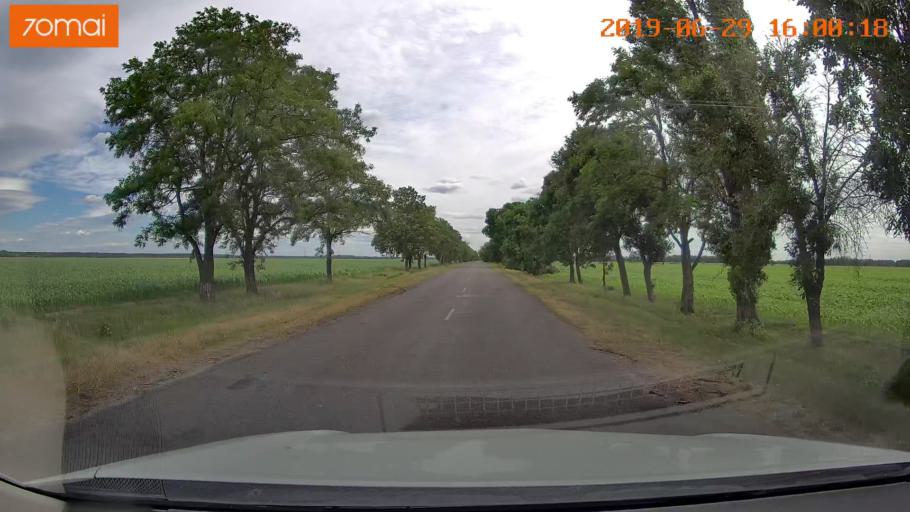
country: BY
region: Brest
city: Luninyets
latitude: 52.2620
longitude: 27.0175
